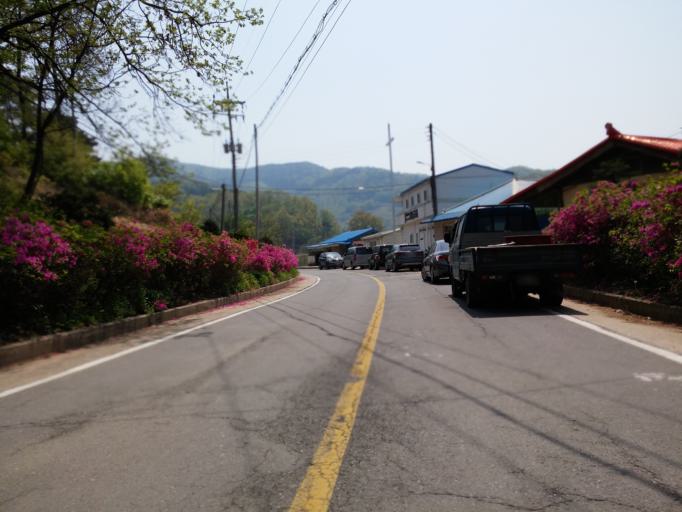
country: KR
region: Chungcheongbuk-do
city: Okcheon
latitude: 36.4481
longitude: 127.5827
